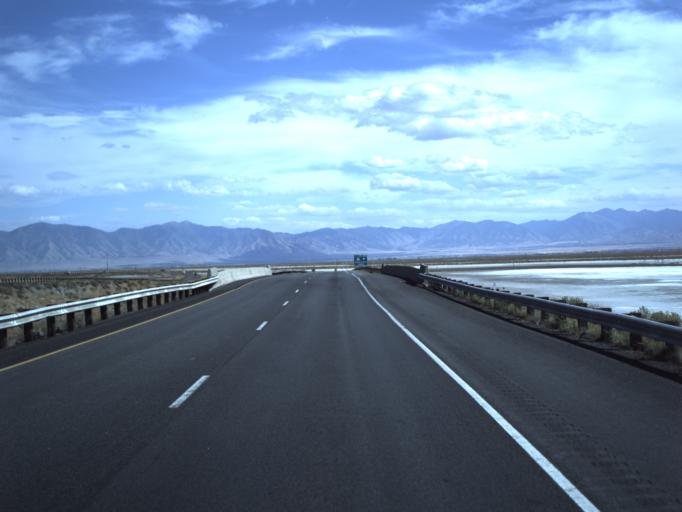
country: US
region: Utah
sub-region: Tooele County
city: Grantsville
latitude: 40.7096
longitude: -112.5307
